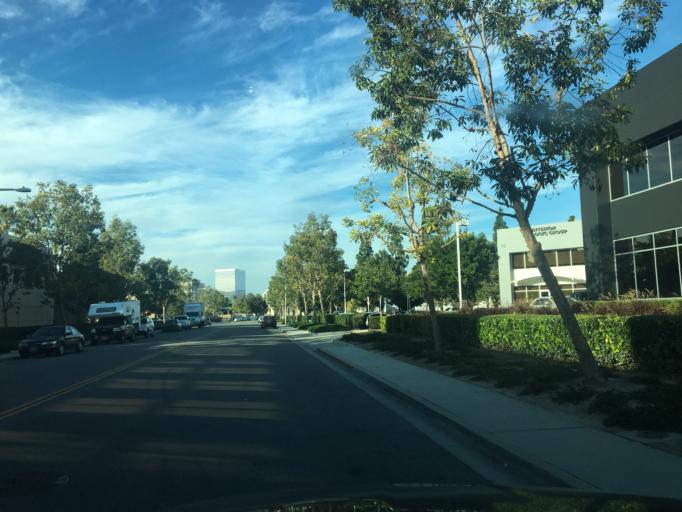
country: US
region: California
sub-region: Orange County
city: Laguna Woods
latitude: 33.6428
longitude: -117.7418
